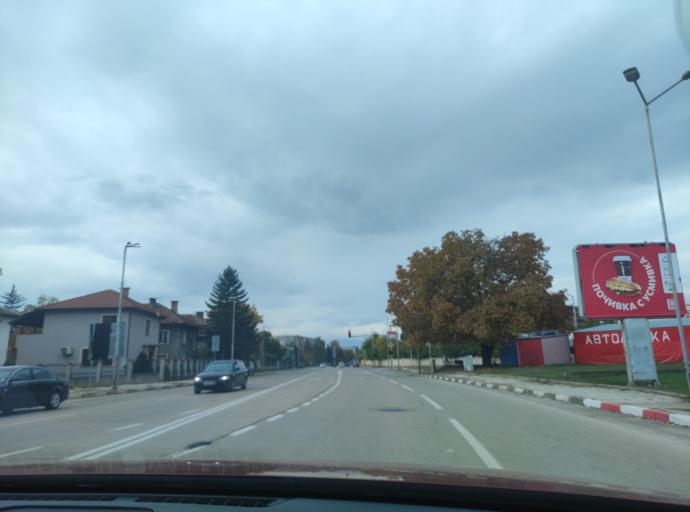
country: BG
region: Montana
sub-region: Obshtina Montana
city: Montana
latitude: 43.4019
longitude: 23.2373
